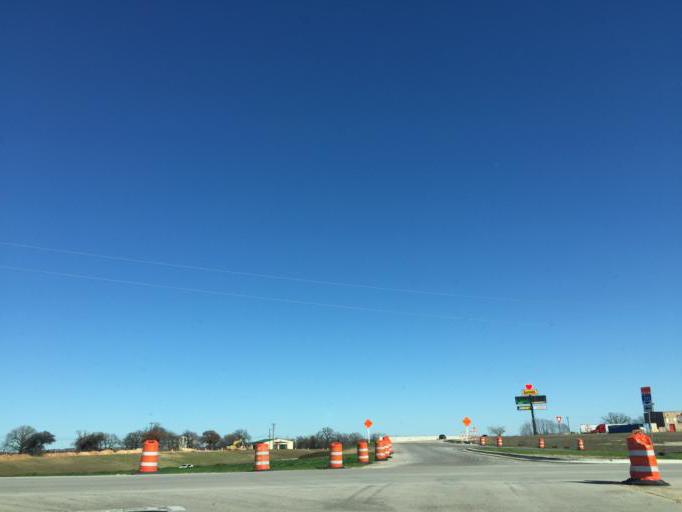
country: US
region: Texas
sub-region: Parker County
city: Hudson Oaks
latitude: 32.7428
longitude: -97.7450
